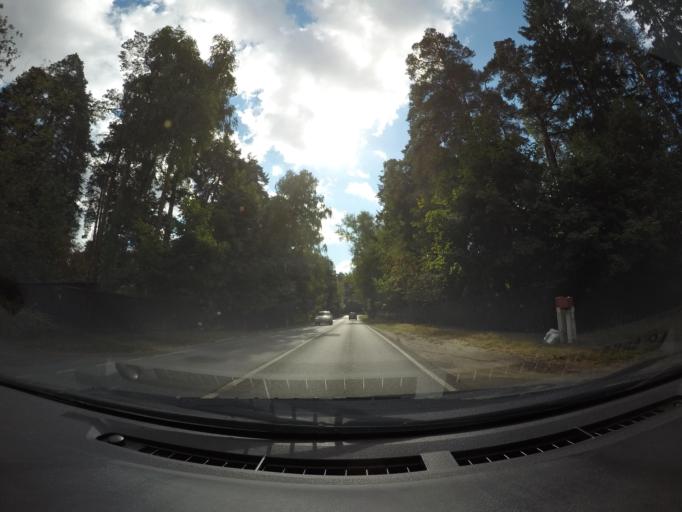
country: RU
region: Moskovskaya
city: Il'inskiy
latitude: 55.6216
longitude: 38.1170
